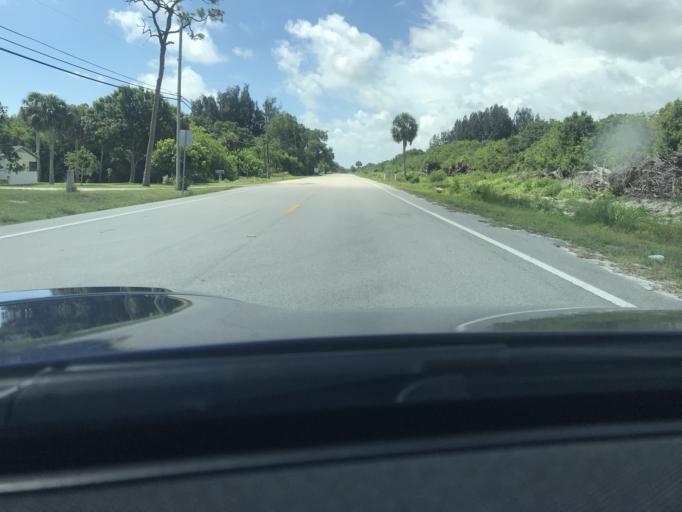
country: US
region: Florida
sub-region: Indian River County
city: Winter Beach
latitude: 27.7403
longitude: -80.4328
